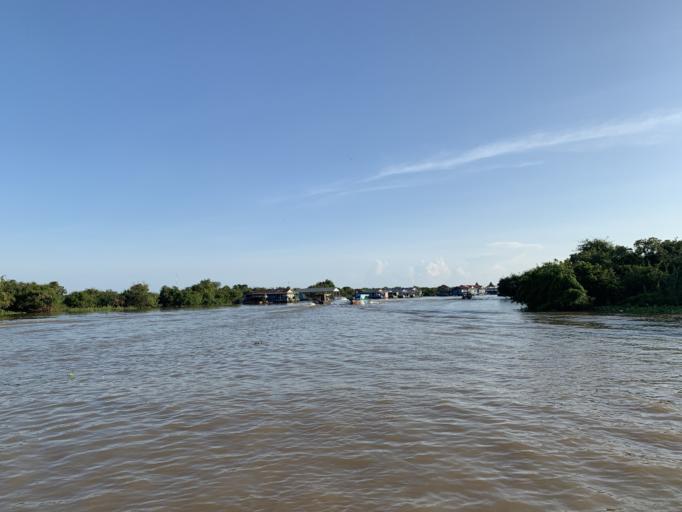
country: KH
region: Siem Reap
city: Siem Reap
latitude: 13.2473
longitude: 103.8232
